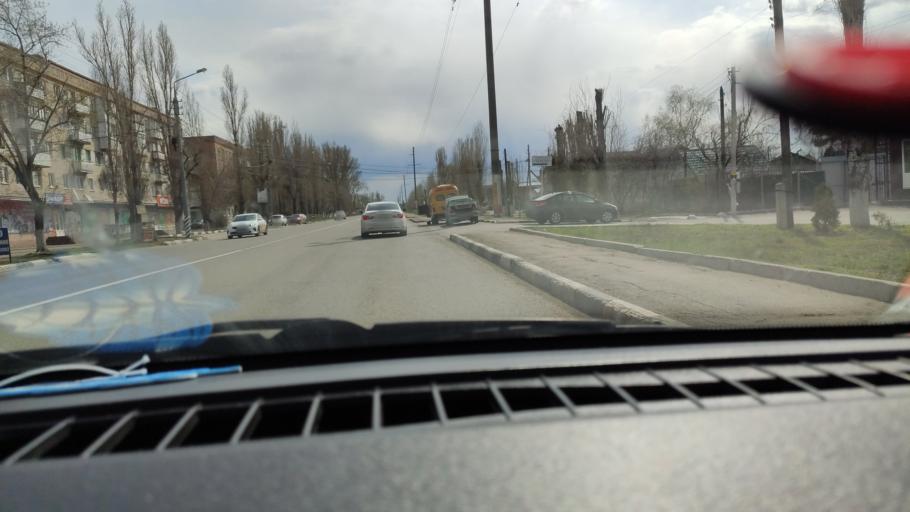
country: RU
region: Saratov
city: Privolzhskiy
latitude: 51.4041
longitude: 46.0381
